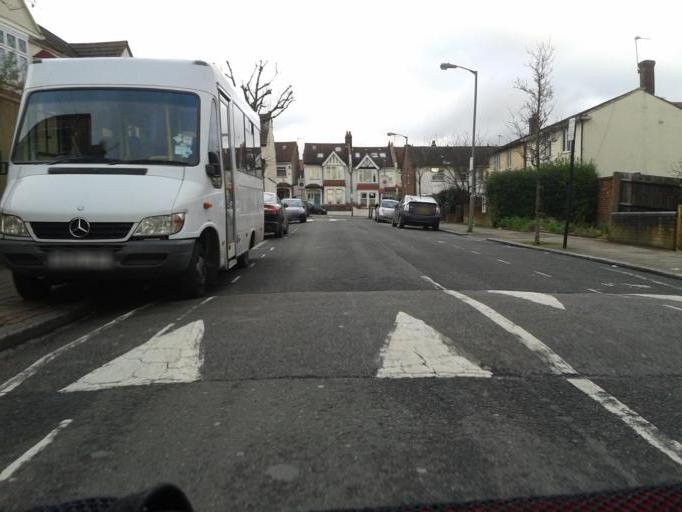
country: GB
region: England
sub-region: Greater London
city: Earlsfield
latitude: 51.4346
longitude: -0.1643
